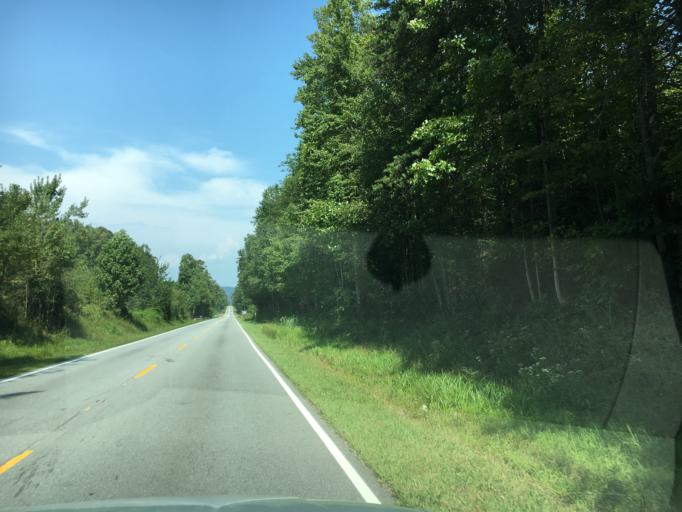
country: US
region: North Carolina
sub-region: McDowell County
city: West Marion
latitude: 35.5918
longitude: -81.9834
